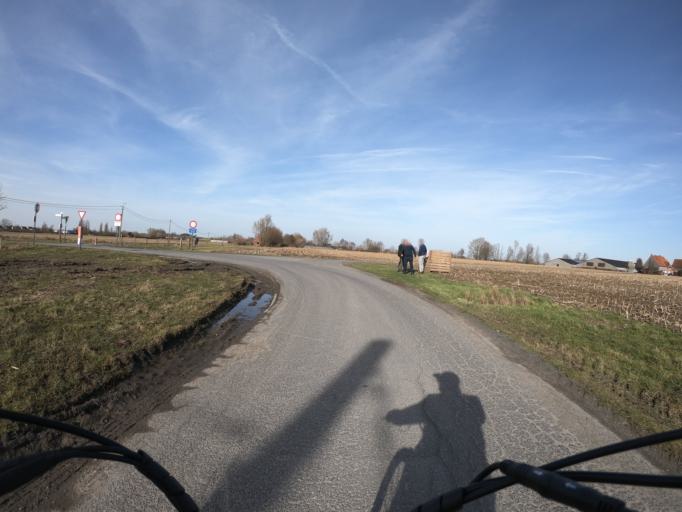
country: BE
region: Flanders
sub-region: Provincie West-Vlaanderen
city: Menen
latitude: 50.8221
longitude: 3.1254
